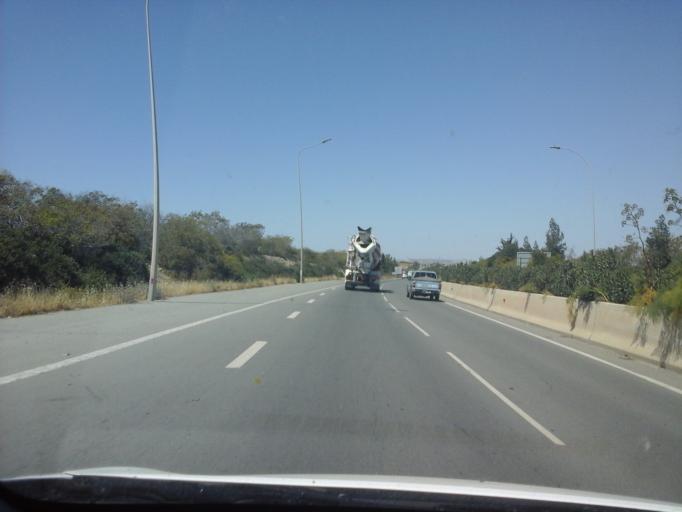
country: CY
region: Lefkosia
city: Kato Deftera
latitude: 35.1297
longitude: 33.2917
